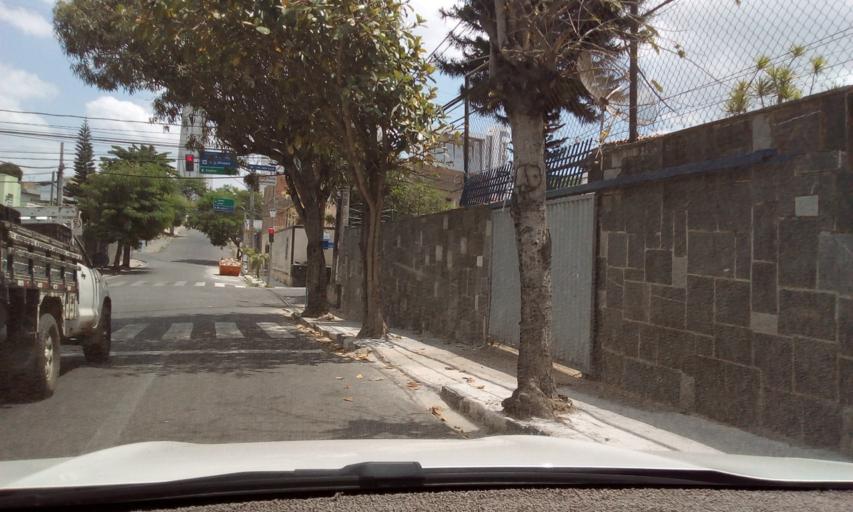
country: BR
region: Pernambuco
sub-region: Caruaru
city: Caruaru
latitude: -8.2779
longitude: -35.9698
